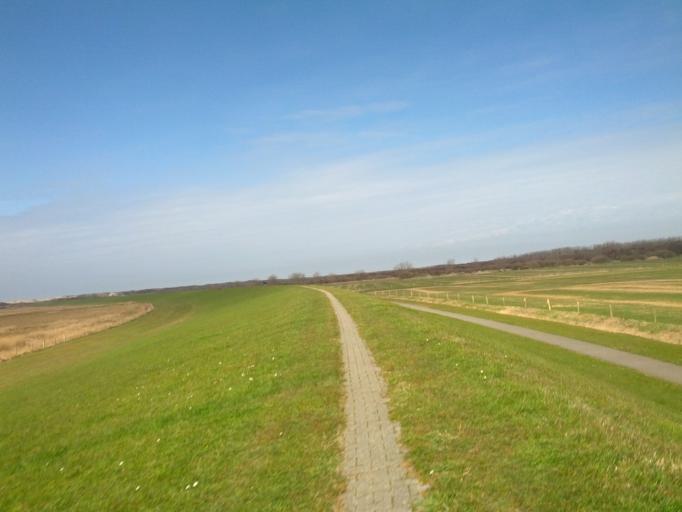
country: DE
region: Lower Saxony
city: Langeoog
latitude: 53.7279
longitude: 7.4862
